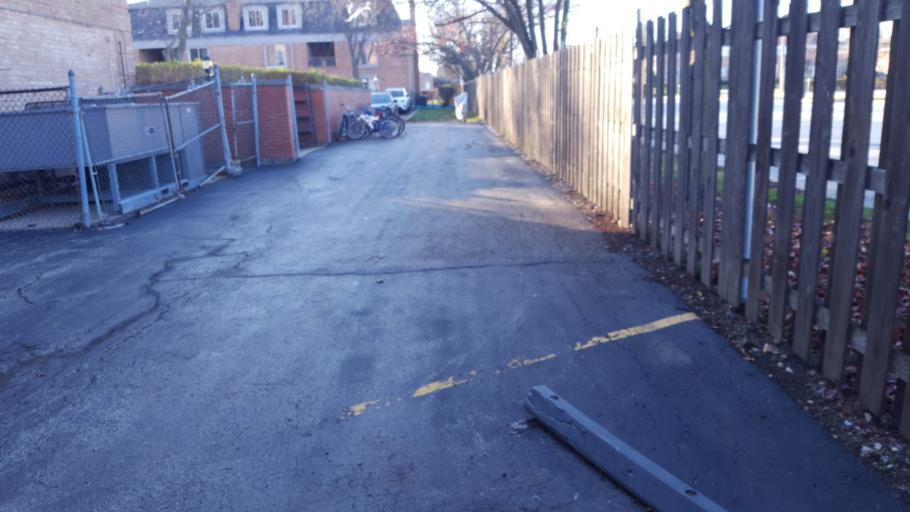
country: US
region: Illinois
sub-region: Cook County
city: Northbrook
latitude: 42.1258
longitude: -87.8281
